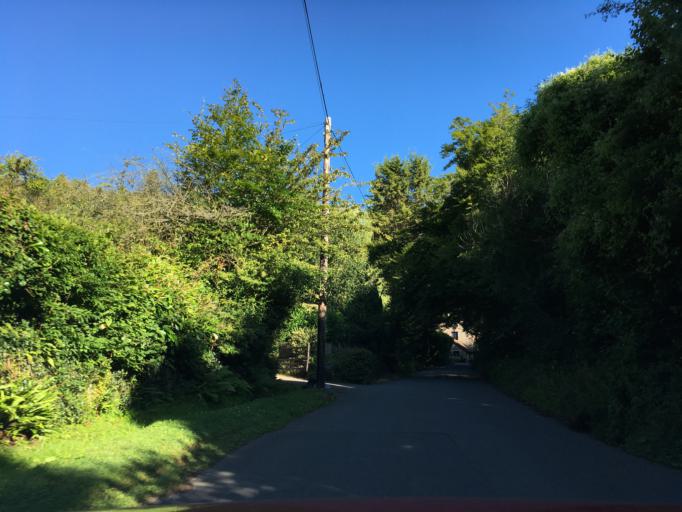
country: GB
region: Wales
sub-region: Monmouthshire
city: Tintern
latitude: 51.7121
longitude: -2.6877
